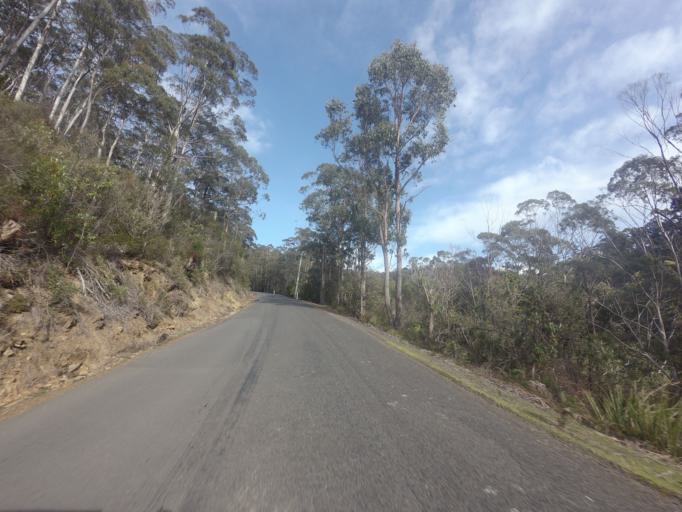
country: AU
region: Tasmania
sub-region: Kingborough
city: Margate
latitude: -43.0010
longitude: 147.1762
